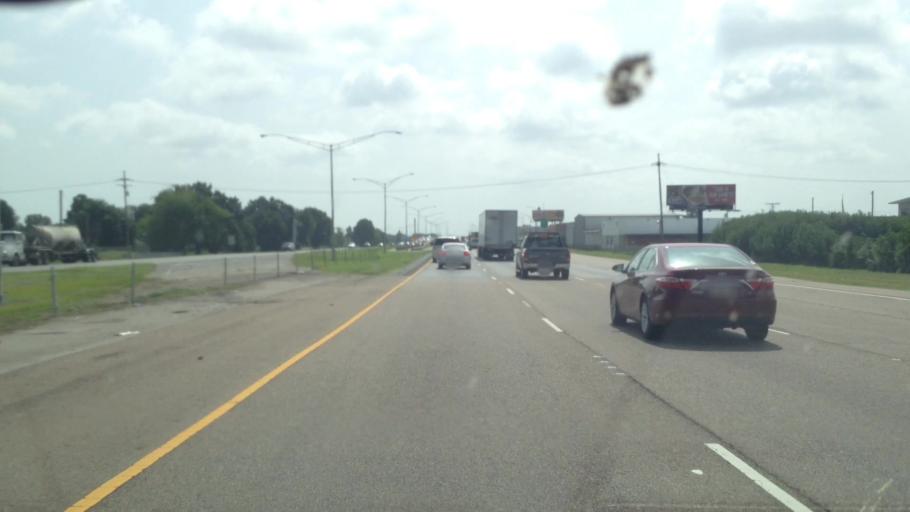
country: US
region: Louisiana
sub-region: Jefferson Parish
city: Kenner
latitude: 30.0068
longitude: -90.2763
